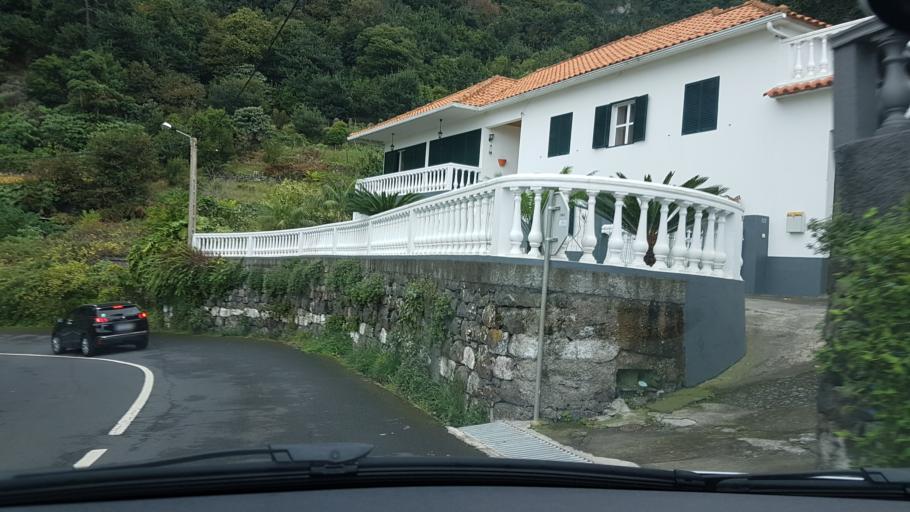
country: PT
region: Madeira
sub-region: Santana
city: Santana
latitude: 32.8240
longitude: -16.9559
